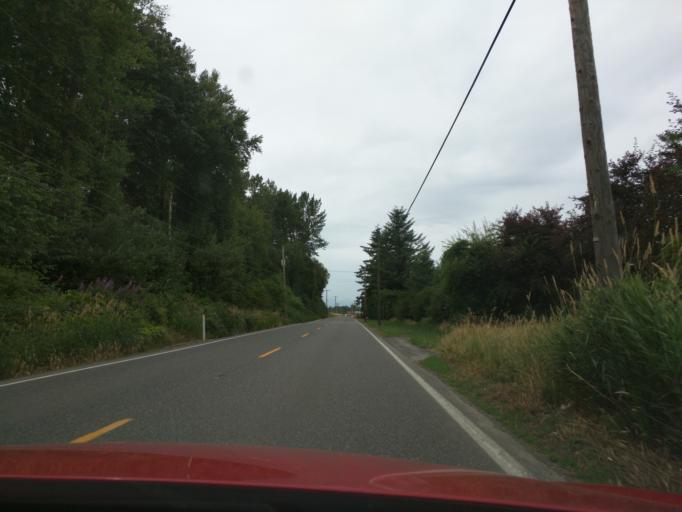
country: US
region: Washington
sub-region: Whatcom County
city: Nooksack
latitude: 48.8961
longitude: -122.3205
